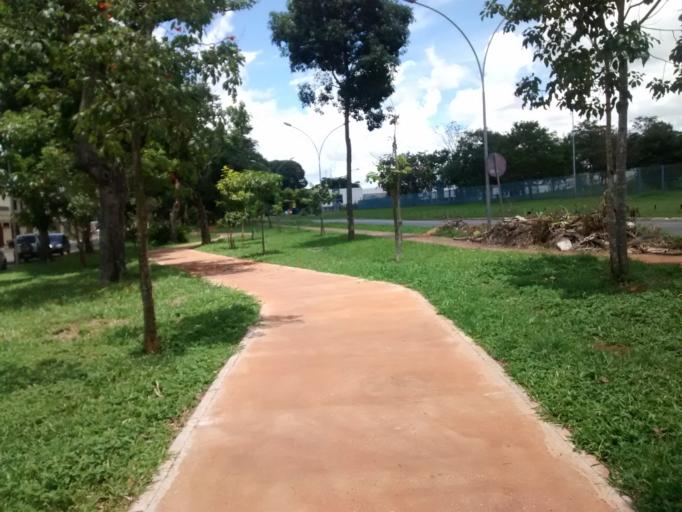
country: BR
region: Federal District
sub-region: Brasilia
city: Brasilia
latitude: -15.8009
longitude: -47.8974
